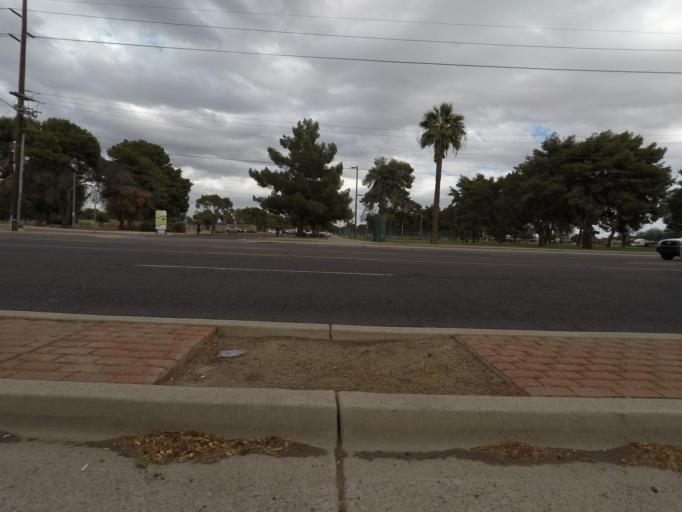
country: US
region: Arizona
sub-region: Maricopa County
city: Glendale
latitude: 33.5033
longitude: -112.1344
